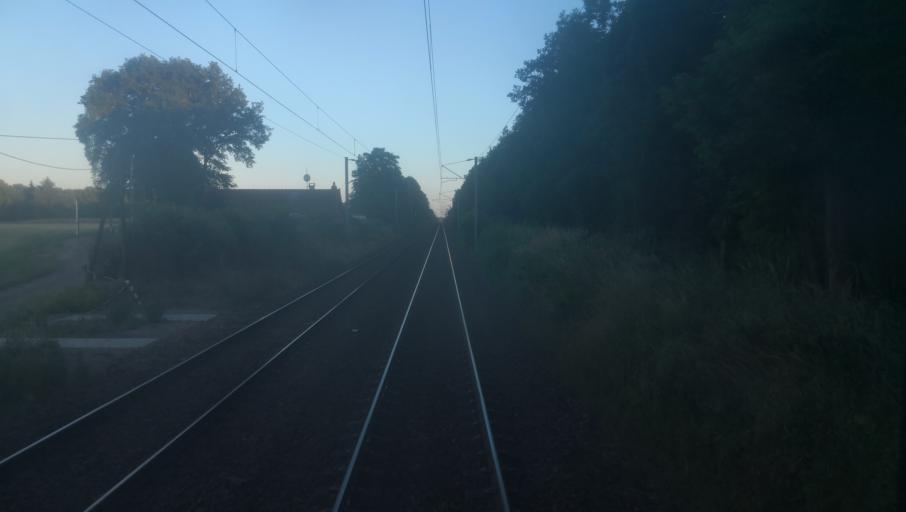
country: FR
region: Bourgogne
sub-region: Departement de la Nievre
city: La Charite-sur-Loire
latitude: 47.2223
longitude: 3.0167
